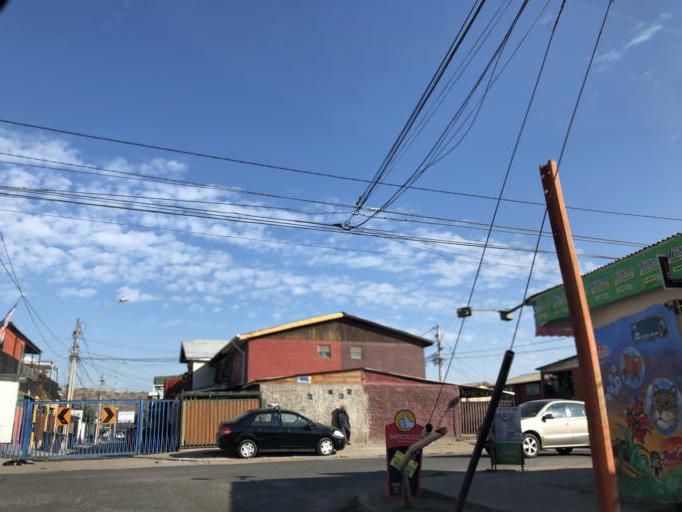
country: CL
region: Santiago Metropolitan
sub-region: Provincia de Cordillera
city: Puente Alto
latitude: -33.6227
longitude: -70.5920
